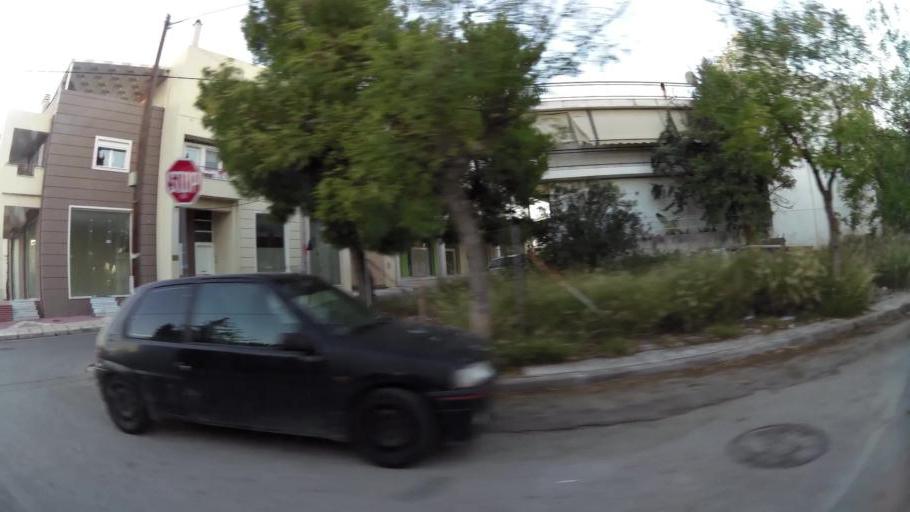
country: GR
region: Attica
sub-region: Nomarchia Dytikis Attikis
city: Ano Liosia
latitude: 38.0839
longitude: 23.7021
